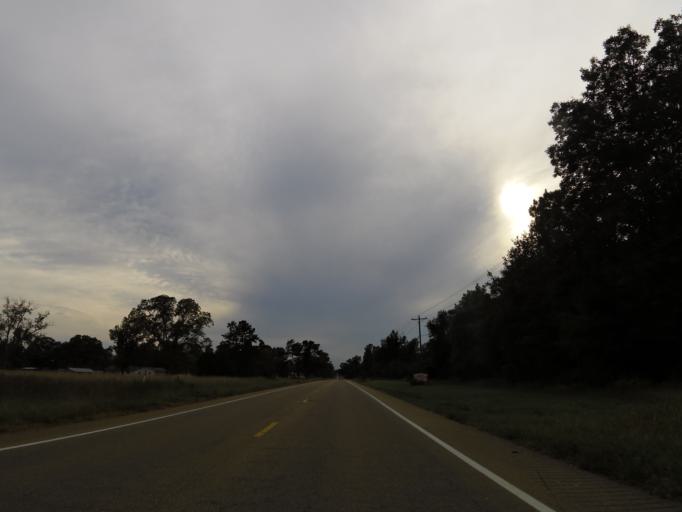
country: US
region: Alabama
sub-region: Monroe County
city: Frisco City
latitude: 31.4475
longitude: -87.3816
